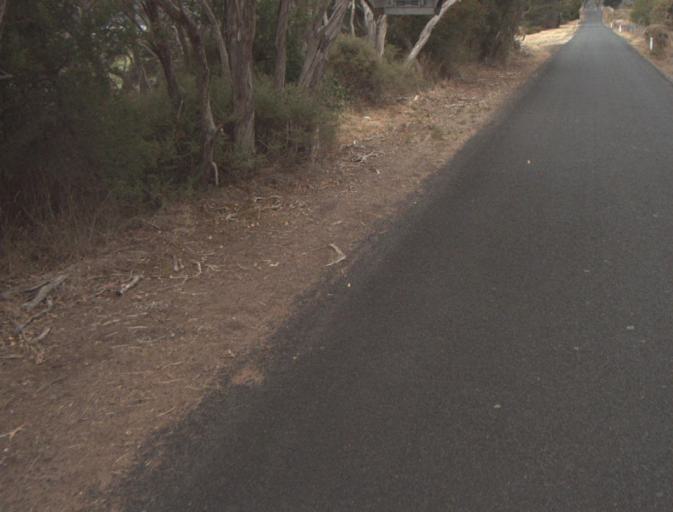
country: AU
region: Tasmania
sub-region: Launceston
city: Mayfield
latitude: -41.2891
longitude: 146.9919
